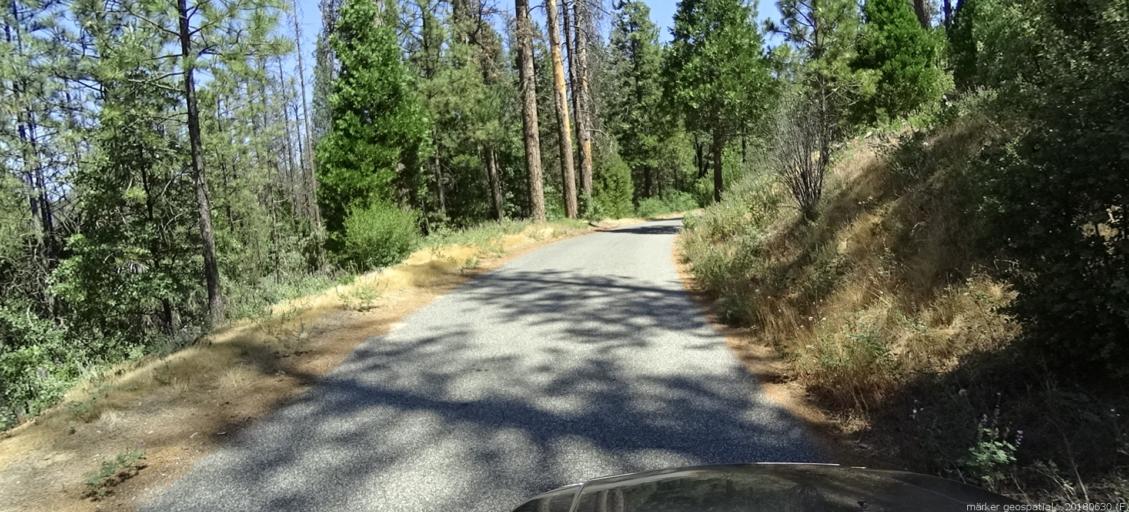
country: US
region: California
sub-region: Madera County
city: Oakhurst
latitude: 37.3562
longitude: -119.3449
